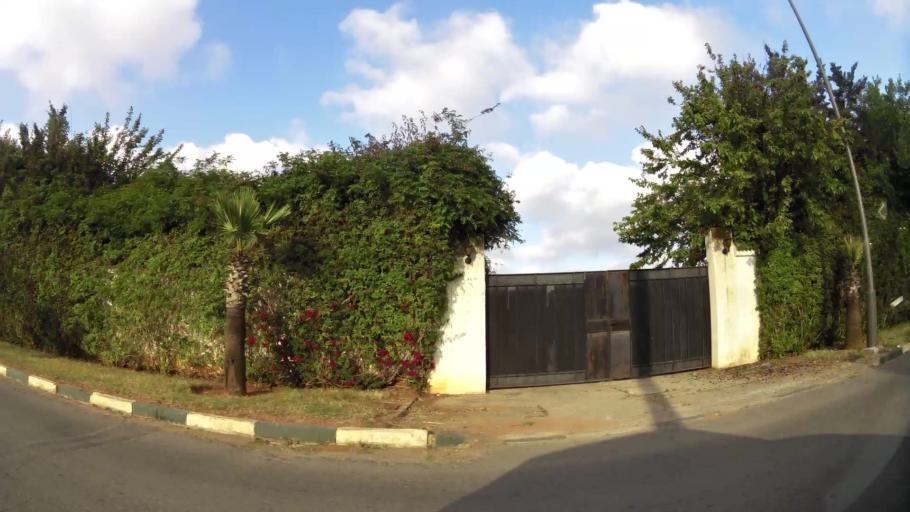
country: MA
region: Rabat-Sale-Zemmour-Zaer
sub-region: Rabat
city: Rabat
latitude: 33.9569
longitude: -6.8417
